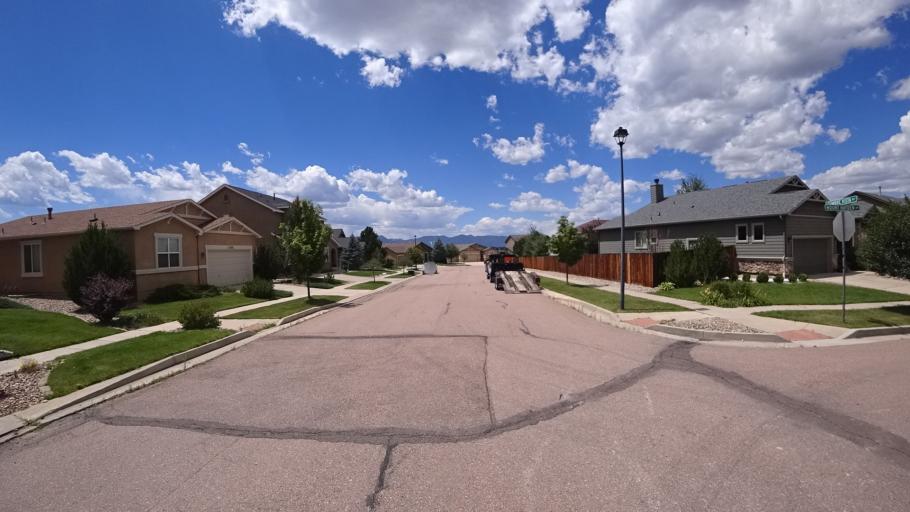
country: US
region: Colorado
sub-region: El Paso County
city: Black Forest
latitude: 38.9466
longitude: -104.7131
